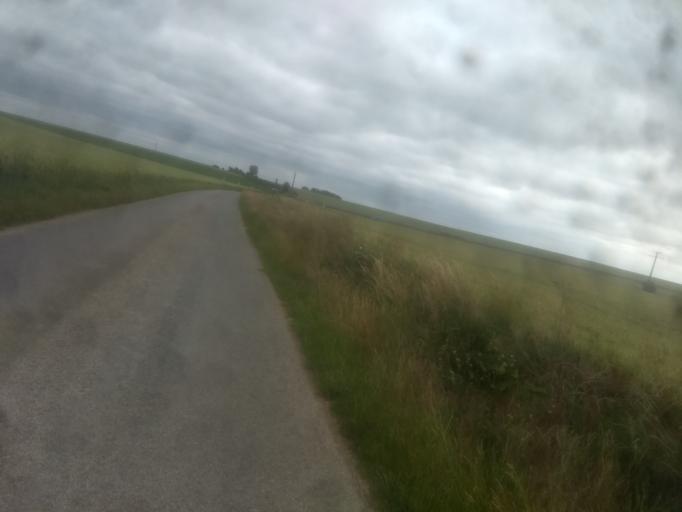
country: FR
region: Nord-Pas-de-Calais
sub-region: Departement du Pas-de-Calais
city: Mont-Saint-Eloi
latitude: 50.3527
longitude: 2.7125
